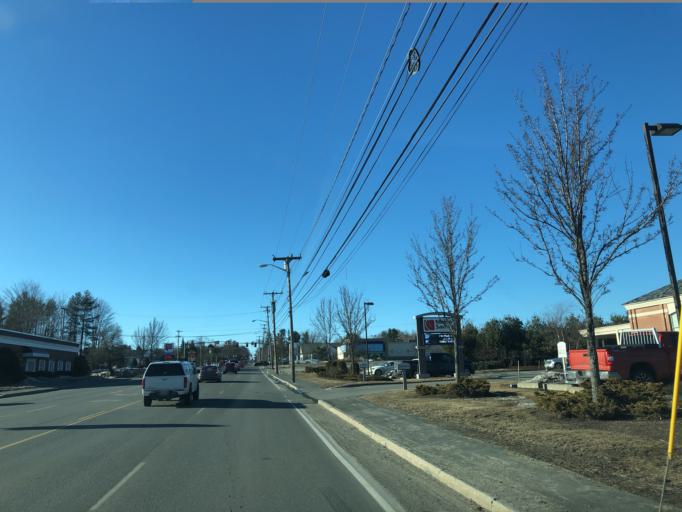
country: US
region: Maine
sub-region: Penobscot County
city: Bangor
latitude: 44.8233
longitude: -68.7792
